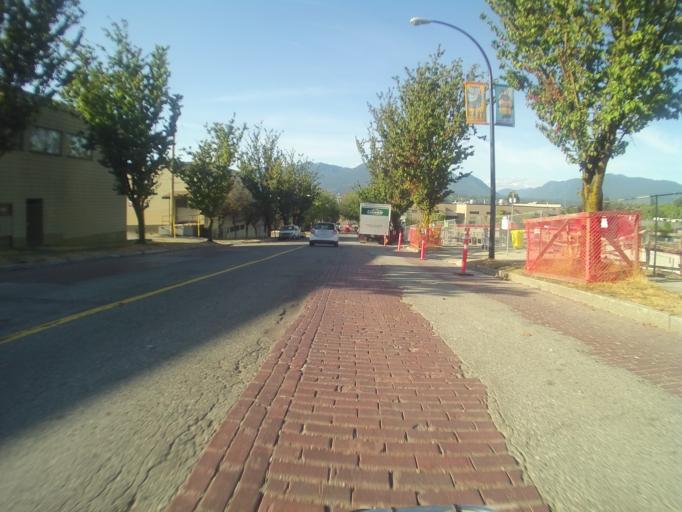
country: CA
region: British Columbia
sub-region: Fraser Valley Regional District
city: North Vancouver
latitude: 49.2824
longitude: -123.0655
